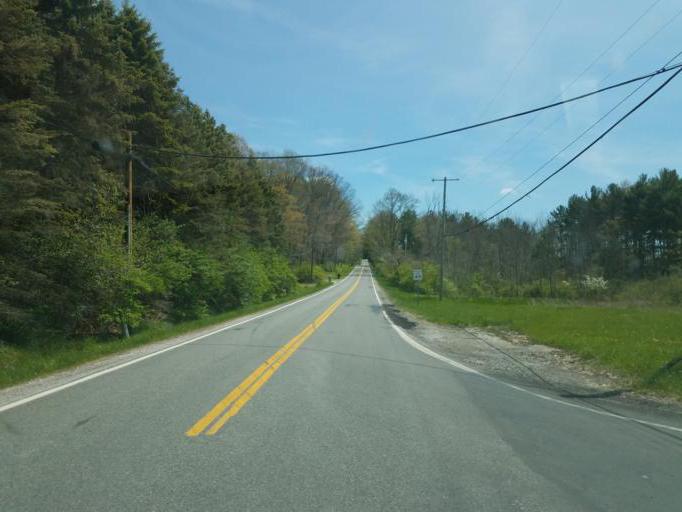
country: US
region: Ohio
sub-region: Summit County
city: Richfield
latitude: 41.2022
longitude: -81.6660
